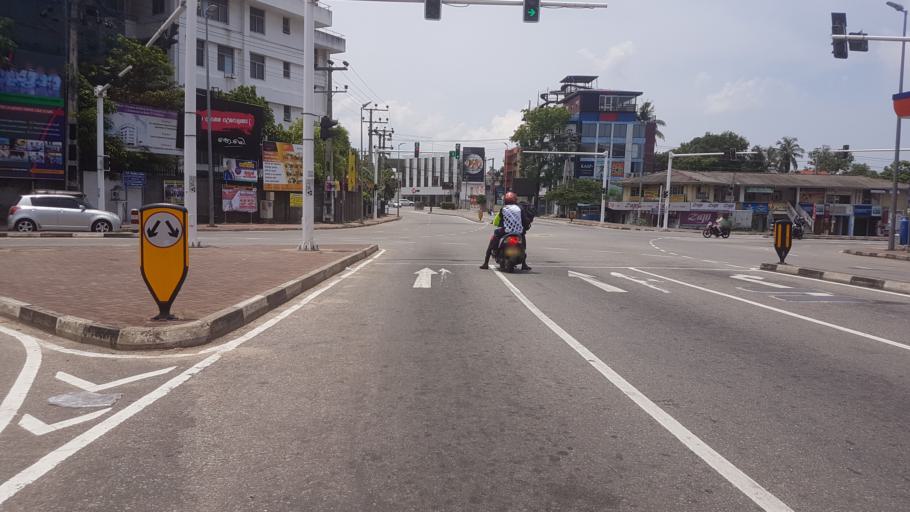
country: LK
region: Western
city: Battaramulla South
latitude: 6.8917
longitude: 79.9289
